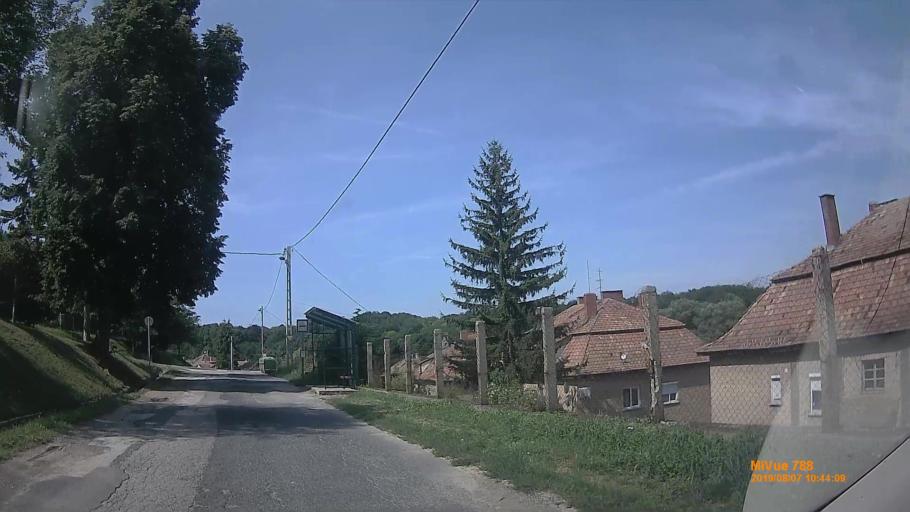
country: HU
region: Veszprem
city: Ajka
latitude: 47.0926
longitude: 17.5863
